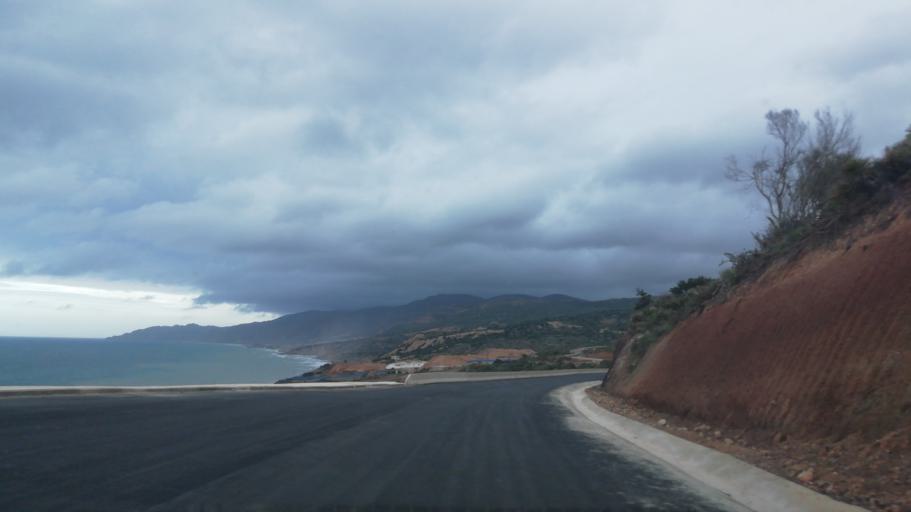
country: DZ
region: Oran
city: Bir el Djir
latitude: 35.7817
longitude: -0.5095
